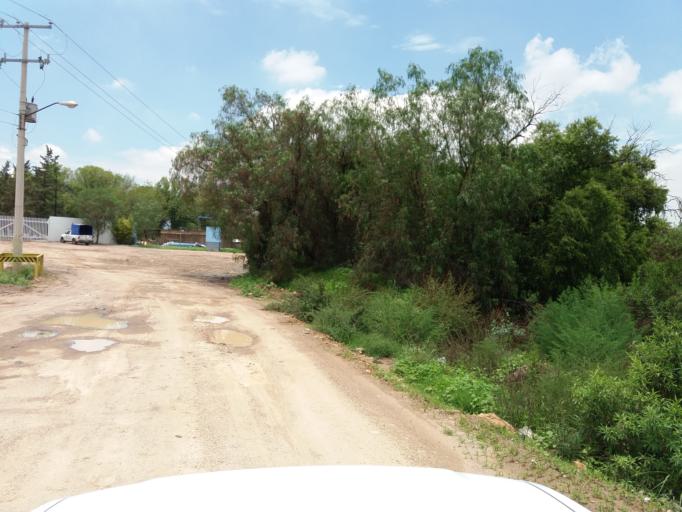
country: MX
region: Aguascalientes
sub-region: Aguascalientes
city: La Loma de los Negritos
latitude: 21.8336
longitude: -102.3370
